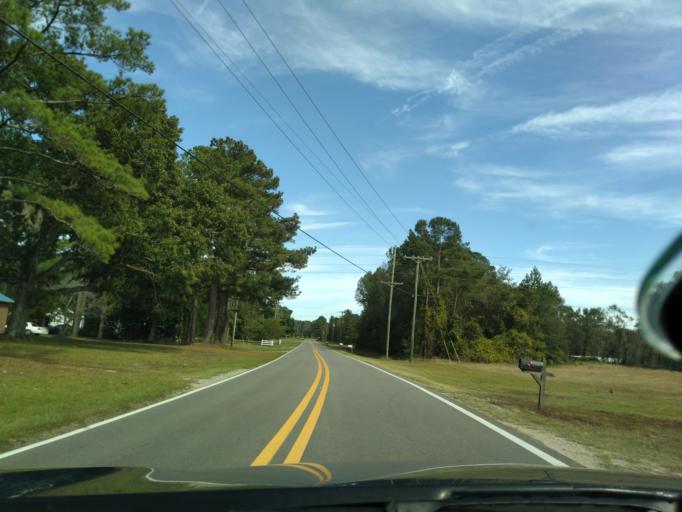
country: US
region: North Carolina
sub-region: Beaufort County
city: River Road
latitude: 35.5042
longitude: -76.9833
